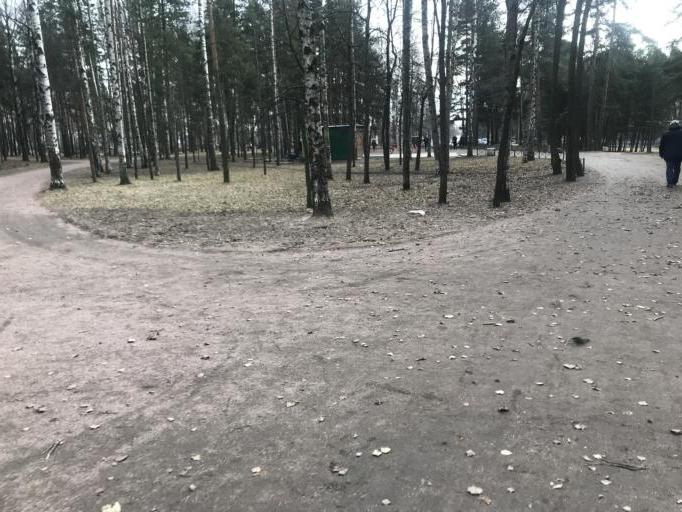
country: RU
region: St.-Petersburg
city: Sosnovka
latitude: 60.0148
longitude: 30.3511
